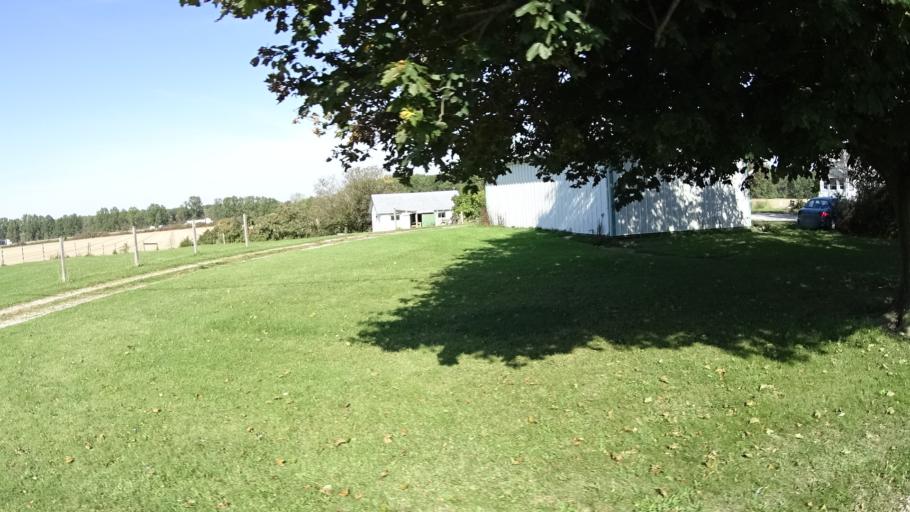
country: US
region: Ohio
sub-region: Lorain County
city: Vermilion-on-the-Lake
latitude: 41.4000
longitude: -82.3050
